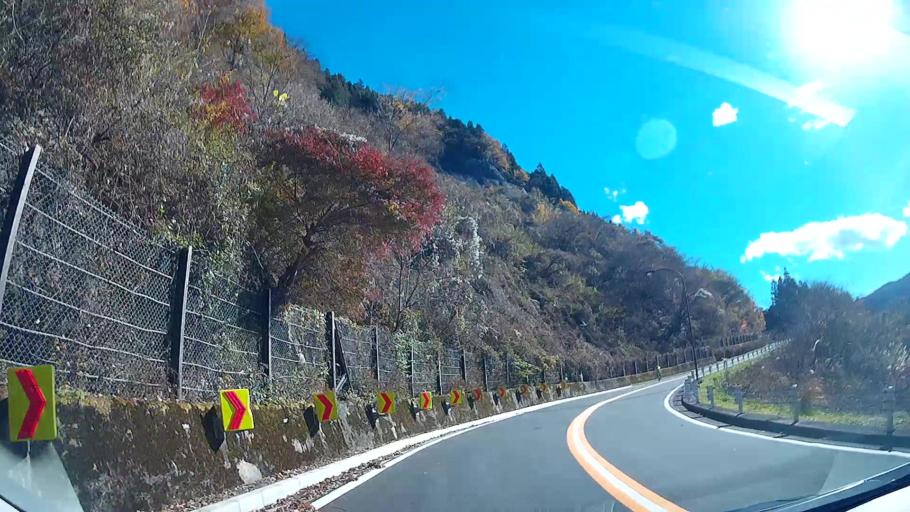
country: JP
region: Yamanashi
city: Uenohara
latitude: 35.7328
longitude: 139.0408
